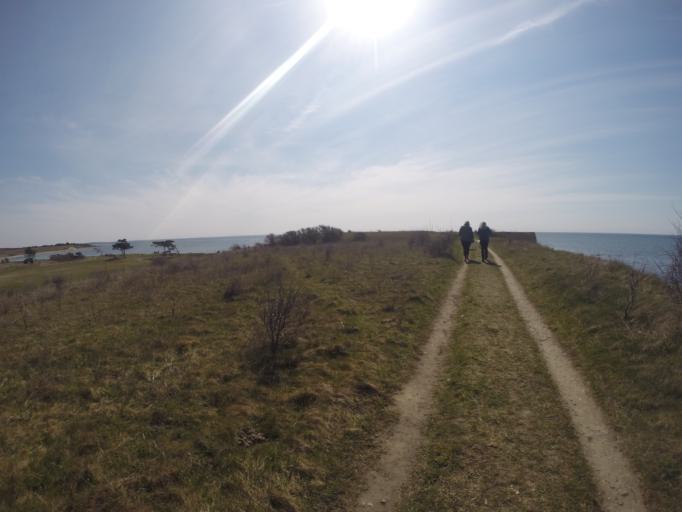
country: DK
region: Zealand
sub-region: Kalundborg Kommune
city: Gorlev
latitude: 55.5160
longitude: 11.0814
